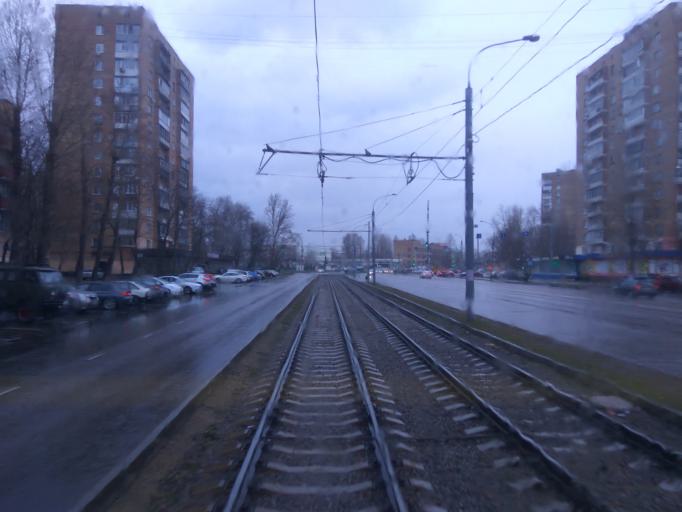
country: RU
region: Moscow
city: Kozeyevo
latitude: 55.8767
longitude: 37.6363
